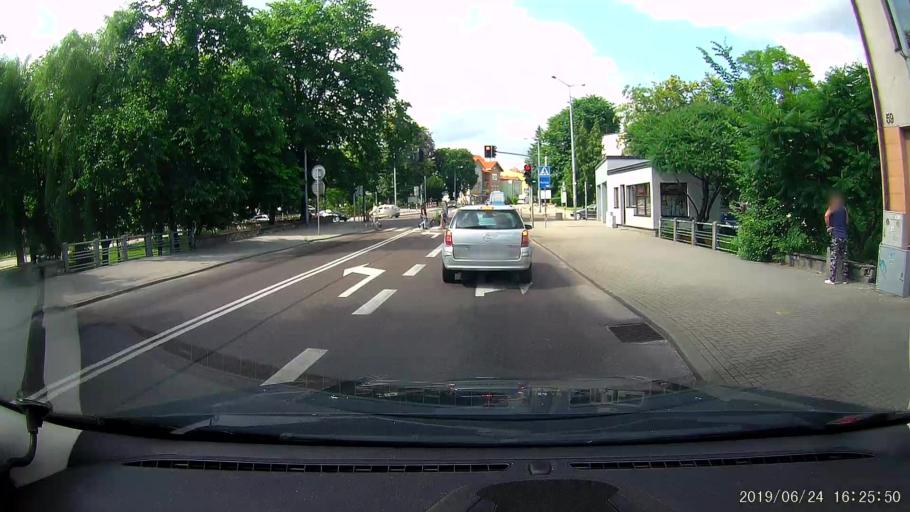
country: PL
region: Lublin Voivodeship
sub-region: Powiat tomaszowski
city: Tomaszow Lubelski
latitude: 50.4461
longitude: 23.4165
